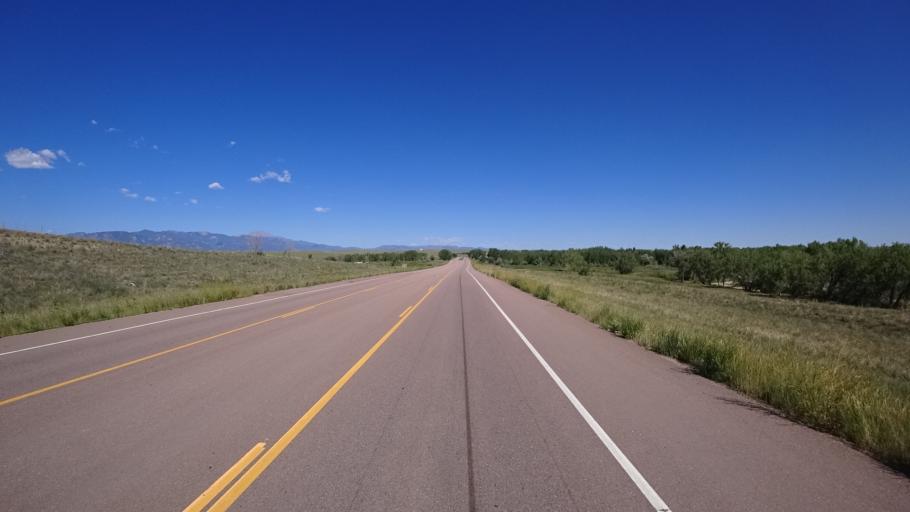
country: US
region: Colorado
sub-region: El Paso County
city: Security-Widefield
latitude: 38.7486
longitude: -104.6502
